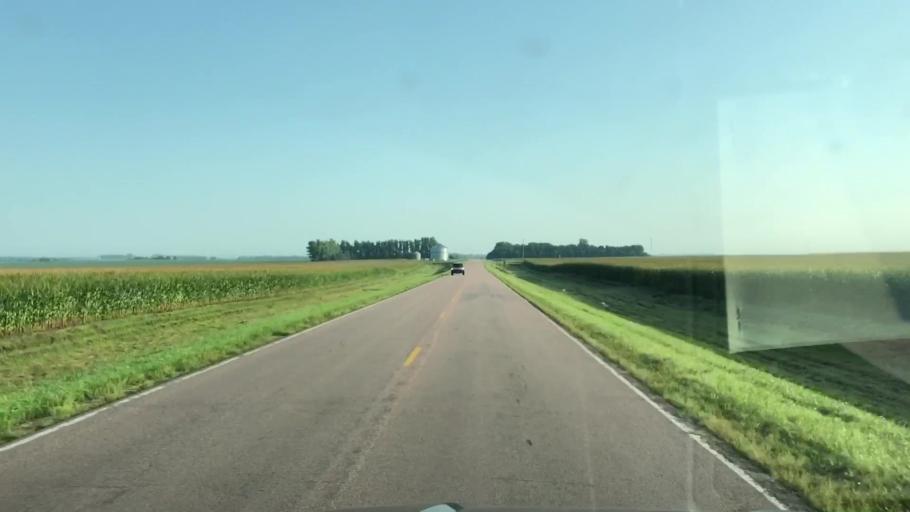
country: US
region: Iowa
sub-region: Lyon County
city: George
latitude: 43.3132
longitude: -95.9990
